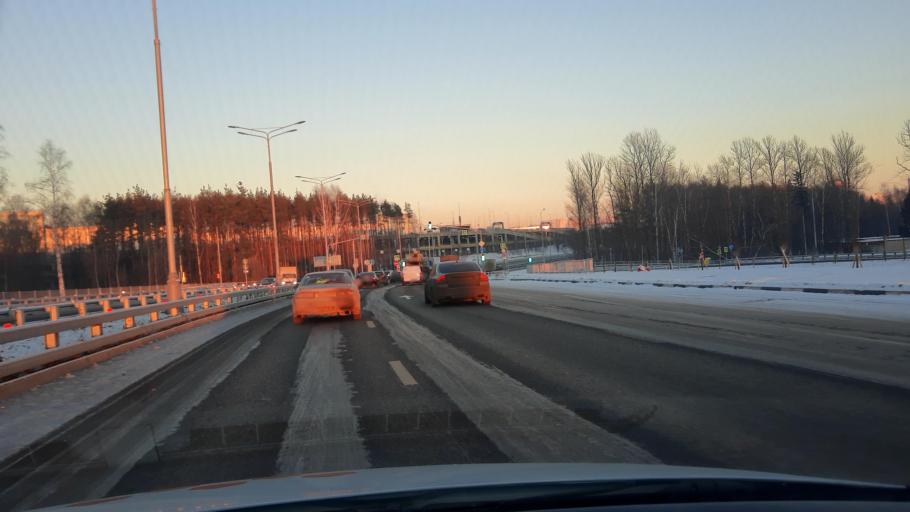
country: RU
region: Moscow
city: Tyoply Stan
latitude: 55.5998
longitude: 37.4871
